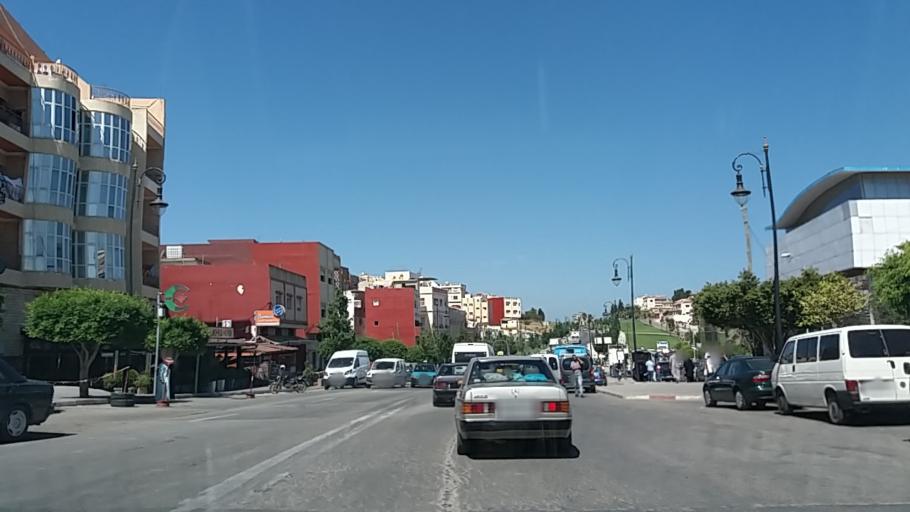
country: MA
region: Tanger-Tetouan
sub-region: Tanger-Assilah
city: Tangier
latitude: 35.7717
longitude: -5.7688
